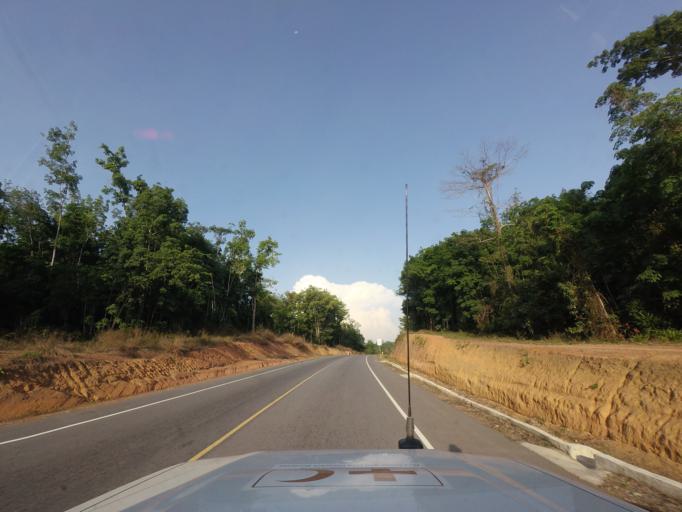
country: LR
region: Bong
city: Gbarnga
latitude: 7.0073
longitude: -9.3893
